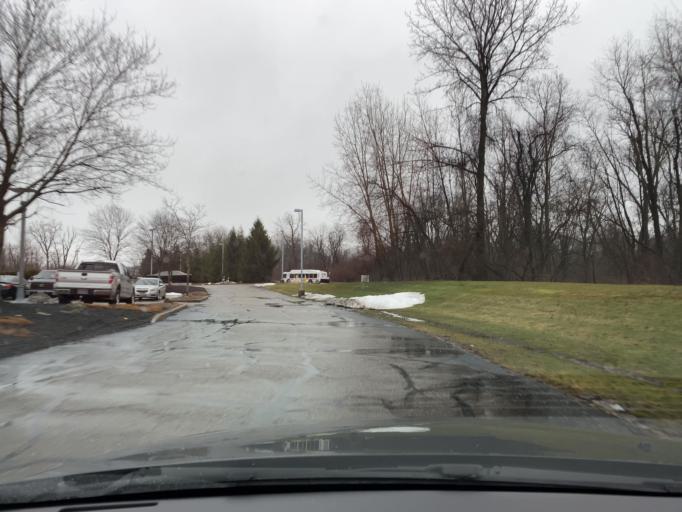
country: US
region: Ohio
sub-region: Summit County
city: Fairlawn
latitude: 41.1019
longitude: -81.5929
